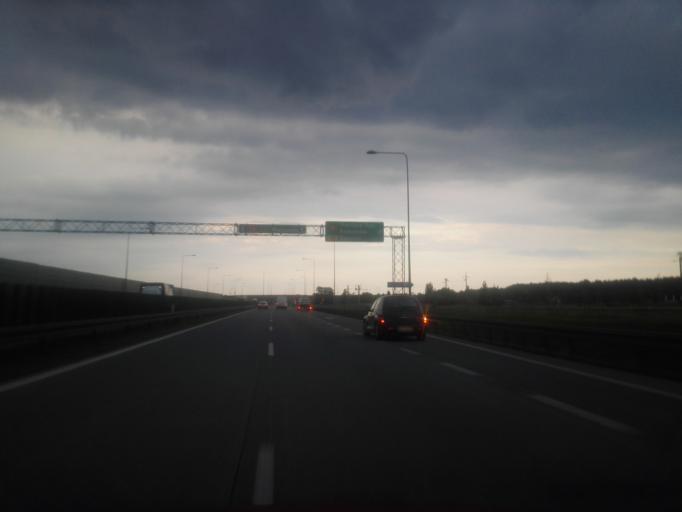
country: PL
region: Lodz Voivodeship
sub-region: Piotrkow Trybunalski
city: Piotrkow Trybunalski
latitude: 51.4437
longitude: 19.7168
